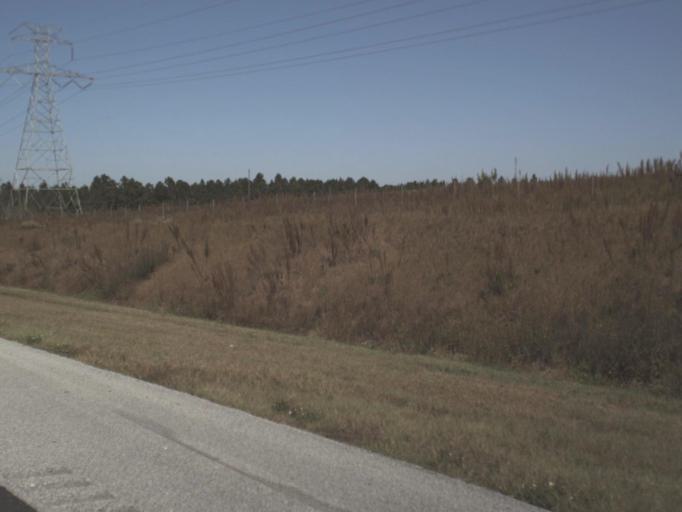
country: US
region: Florida
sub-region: Lake County
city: Hawthorne
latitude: 28.7650
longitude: -81.9487
